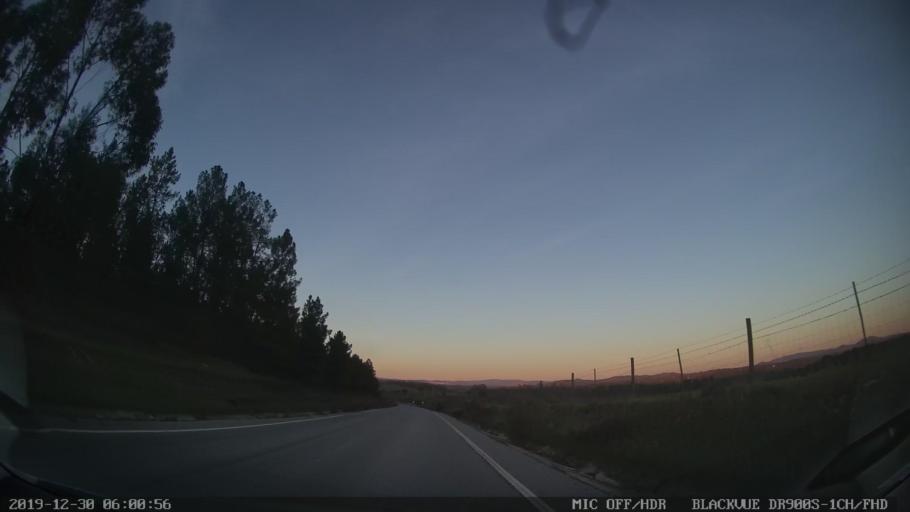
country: PT
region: Castelo Branco
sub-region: Idanha-A-Nova
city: Idanha-a-Nova
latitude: 40.0562
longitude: -7.2445
